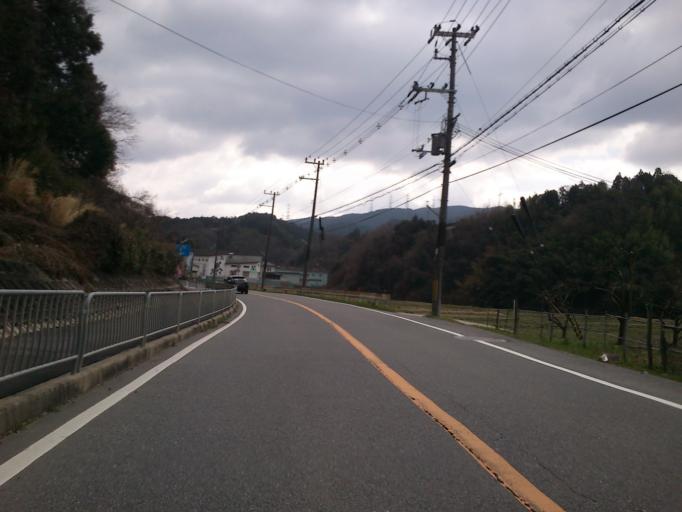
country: JP
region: Kyoto
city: Uji
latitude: 34.8575
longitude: 135.8915
